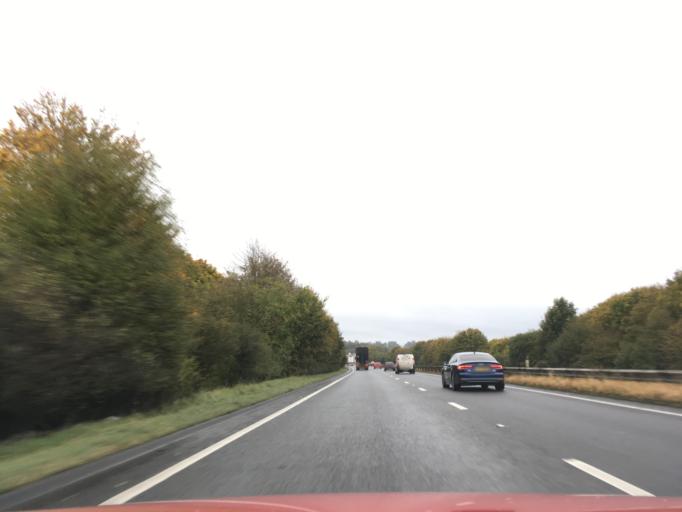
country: GB
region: England
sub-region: Hampshire
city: Kings Worthy
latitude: 51.1435
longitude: -1.3471
